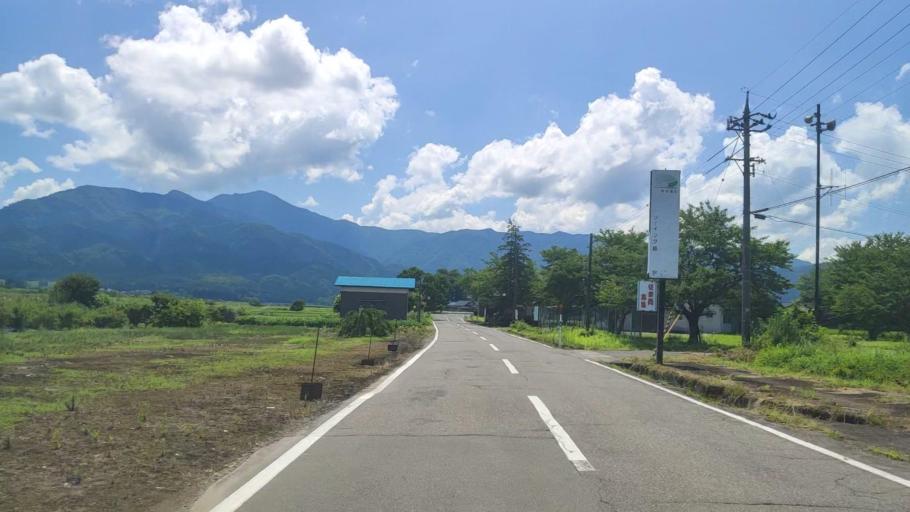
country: JP
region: Fukui
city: Ono
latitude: 35.9703
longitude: 136.5262
